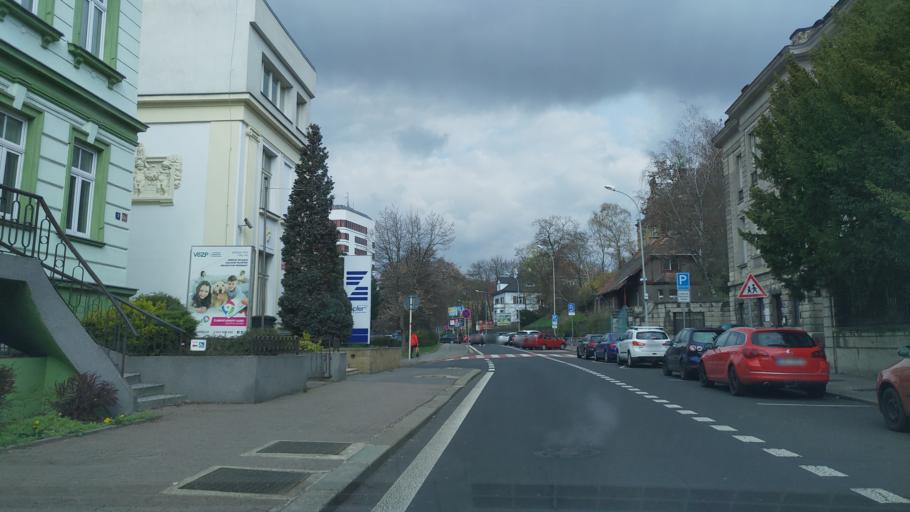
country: CZ
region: Ustecky
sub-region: Okres Usti nad Labem
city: Usti nad Labem
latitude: 50.6636
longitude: 14.0353
